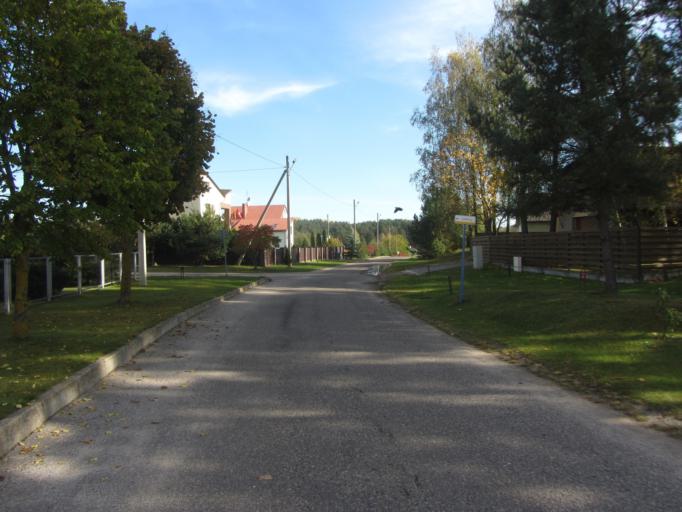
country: LT
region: Vilnius County
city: Elektrenai
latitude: 54.7851
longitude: 24.6963
